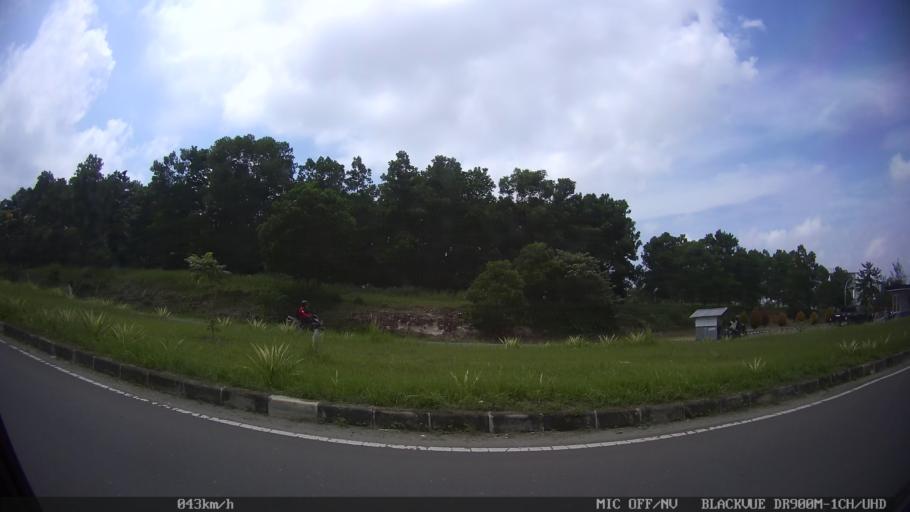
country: ID
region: Lampung
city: Kedaton
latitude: -5.3564
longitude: 105.3154
